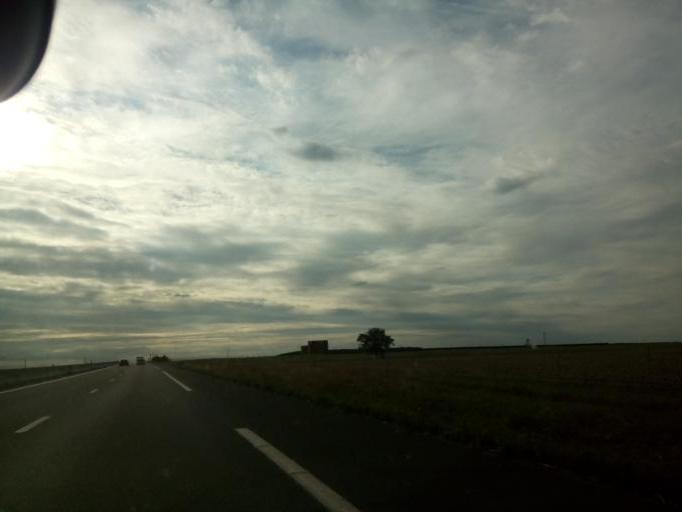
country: FR
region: Centre
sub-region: Departement d'Indre-et-Loire
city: Athee-sur-Cher
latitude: 47.3001
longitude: 0.9144
